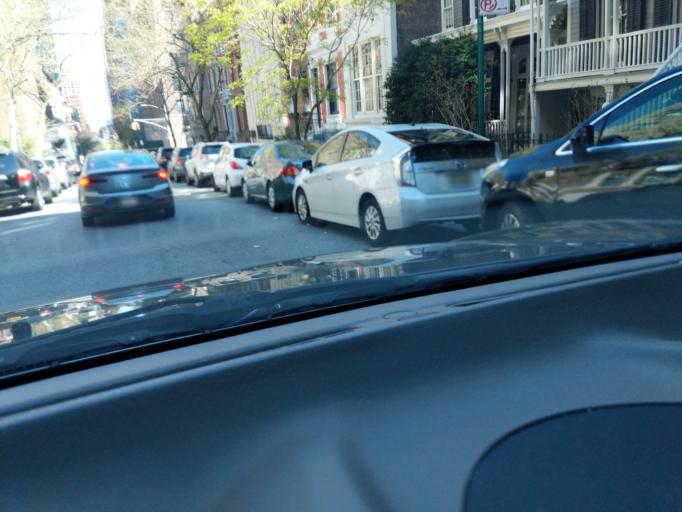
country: US
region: New York
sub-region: New York County
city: Manhattan
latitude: 40.7836
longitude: -73.9536
